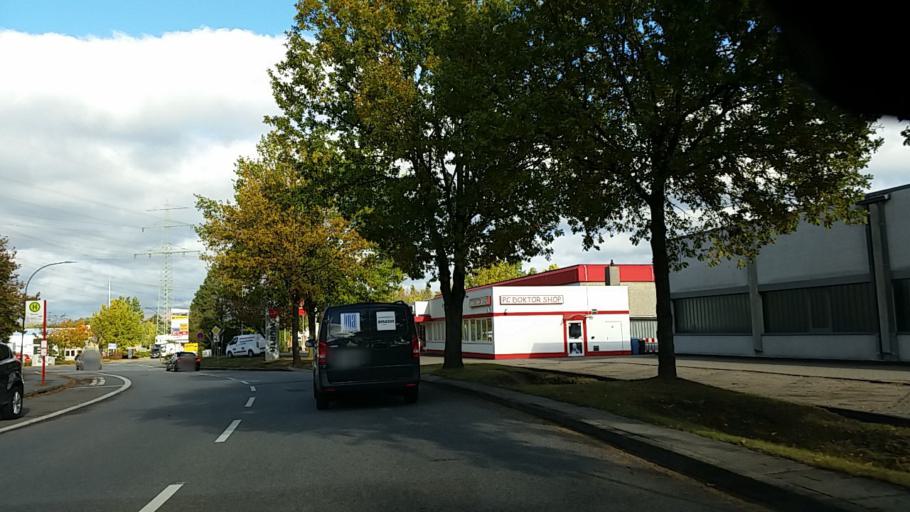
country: DE
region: Schleswig-Holstein
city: Oststeinbek
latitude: 53.5480
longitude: 10.1592
